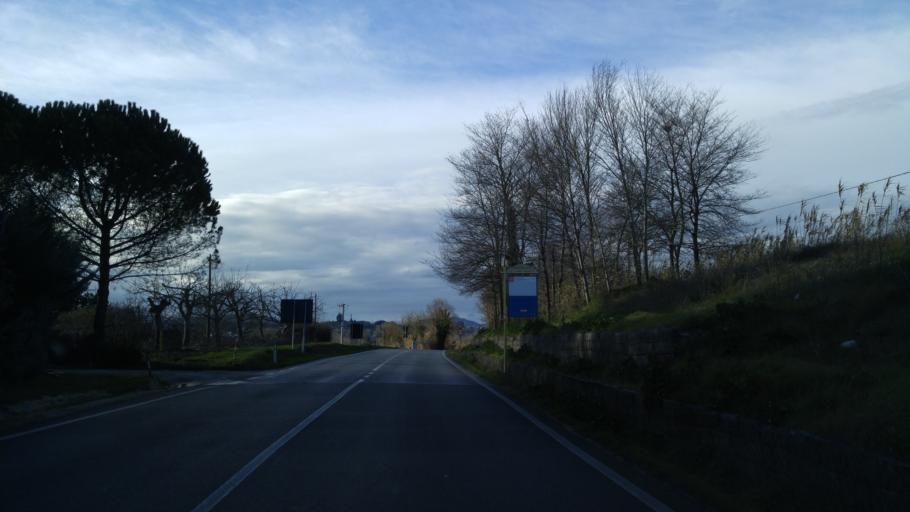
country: IT
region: The Marches
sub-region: Provincia di Ancona
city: Camerano
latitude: 43.5074
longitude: 13.5461
